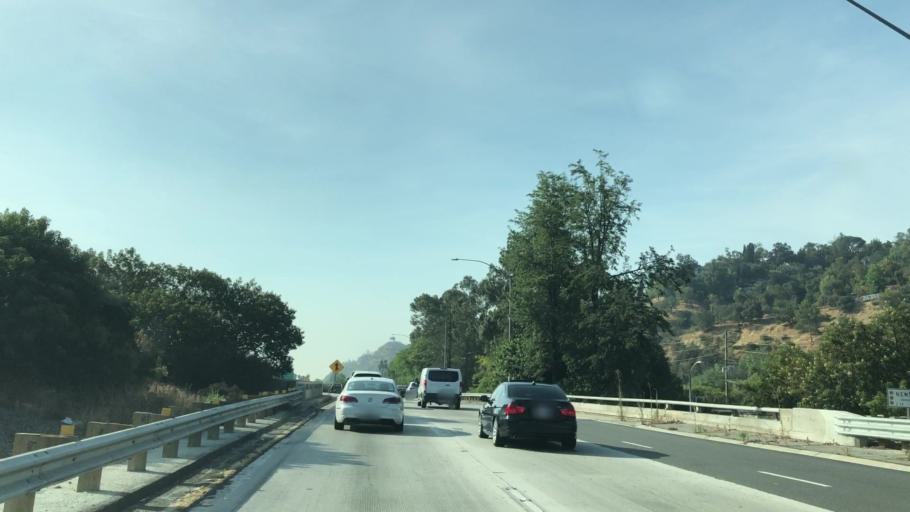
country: US
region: California
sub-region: Los Angeles County
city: Echo Park
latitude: 34.0992
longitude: -118.2480
